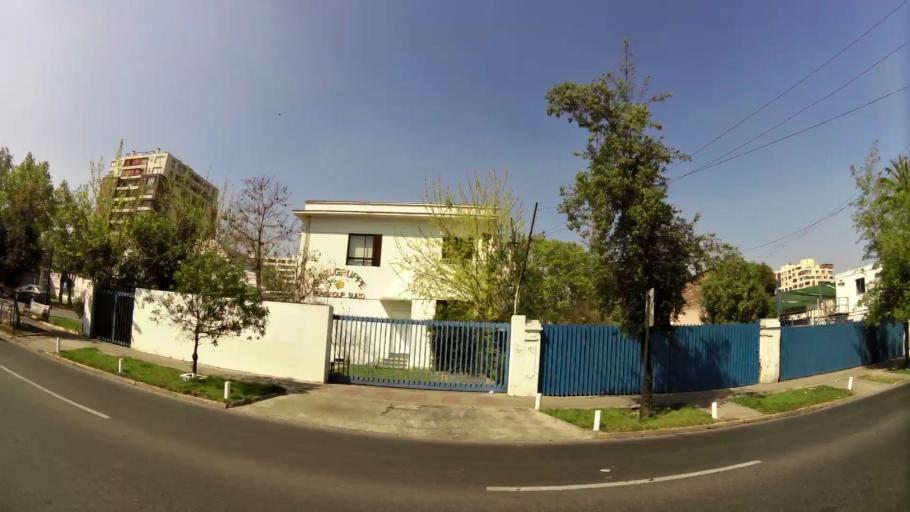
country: CL
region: Santiago Metropolitan
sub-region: Provincia de Santiago
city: Villa Presidente Frei, Nunoa, Santiago, Chile
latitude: -33.4557
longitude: -70.6092
